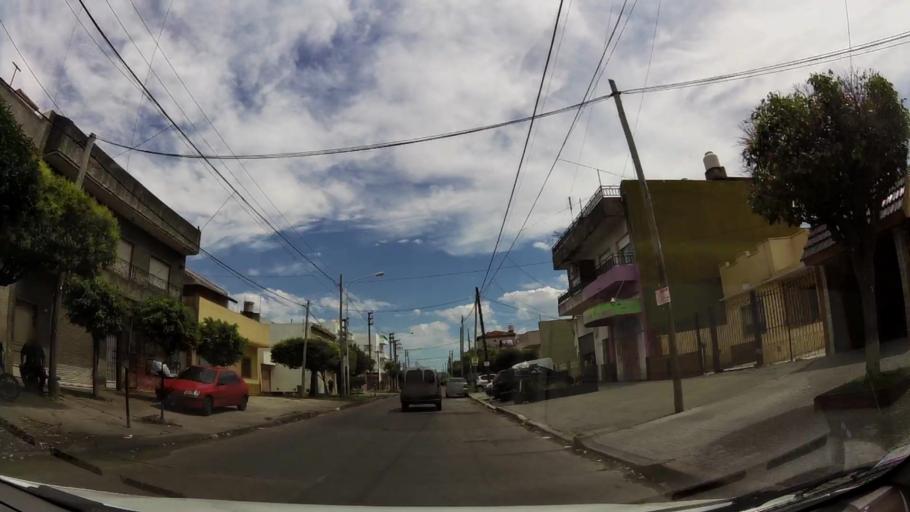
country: AR
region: Buenos Aires
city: San Justo
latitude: -34.6835
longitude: -58.5265
